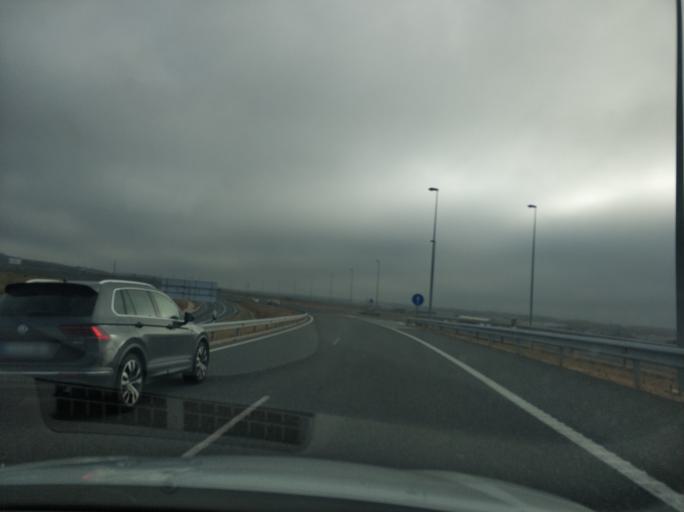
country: ES
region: Castille and Leon
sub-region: Provincia de Leon
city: Leon
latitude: 42.5693
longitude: -5.5449
